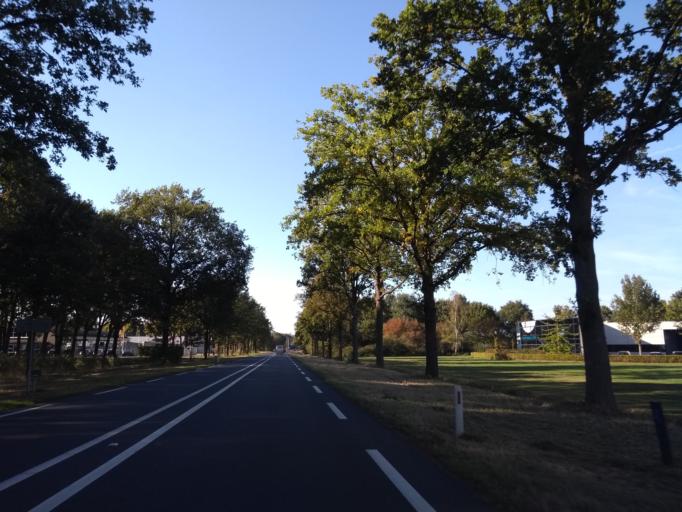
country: NL
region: Overijssel
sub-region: Gemeente Borne
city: Borne
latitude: 52.3084
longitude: 6.7470
